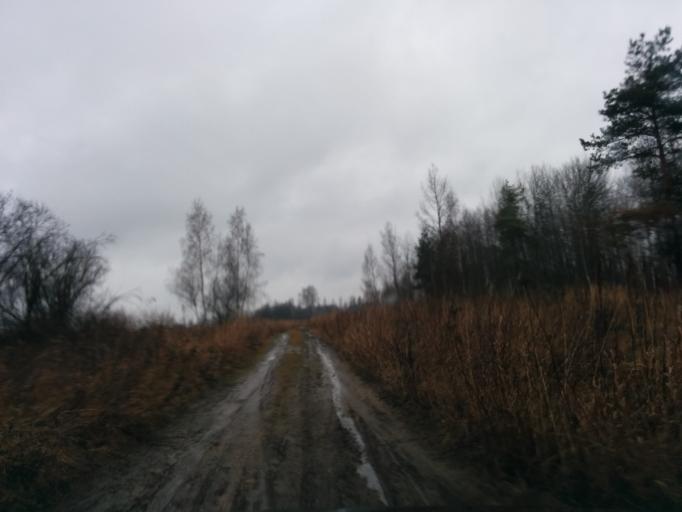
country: LV
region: Jelgava
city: Jelgava
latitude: 56.6776
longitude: 23.7094
